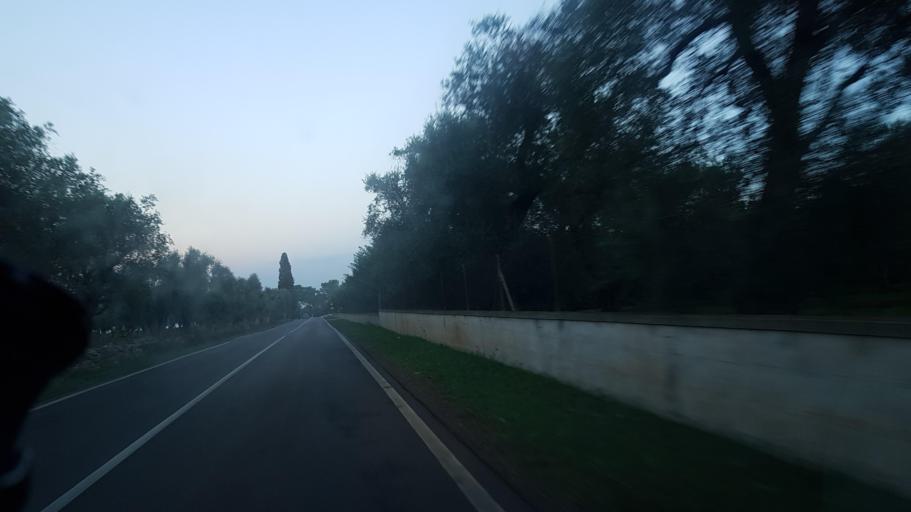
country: IT
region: Apulia
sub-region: Provincia di Brindisi
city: Latiano
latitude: 40.5694
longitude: 17.6841
